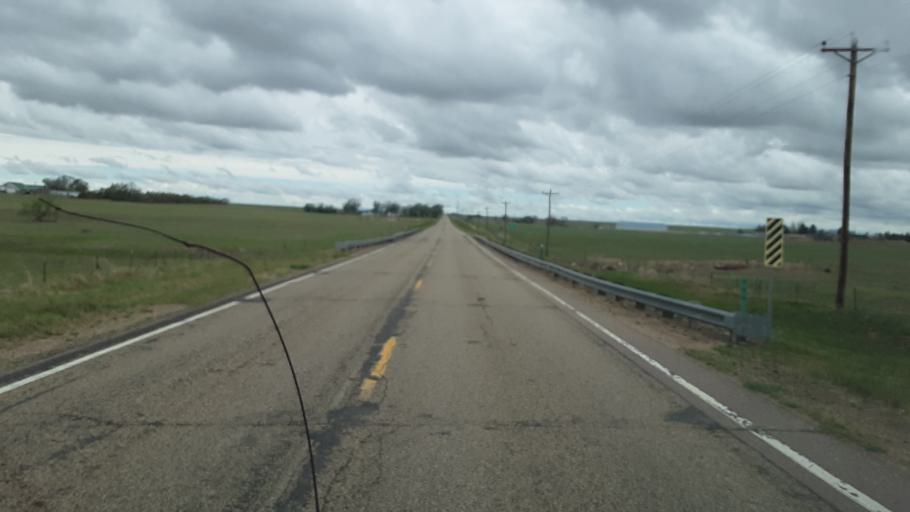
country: US
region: Colorado
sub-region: El Paso County
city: Ellicott
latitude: 38.8398
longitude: -103.9901
